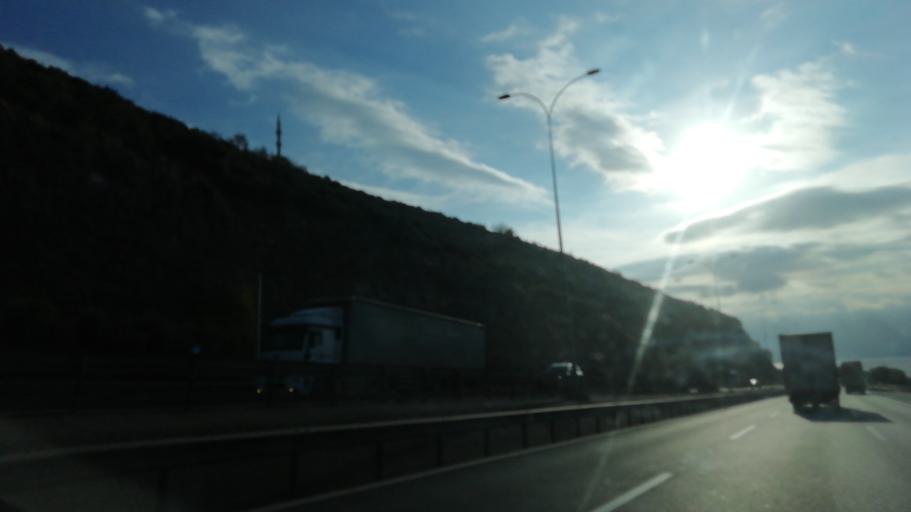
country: TR
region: Kocaeli
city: Hereke
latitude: 40.7825
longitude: 29.6271
